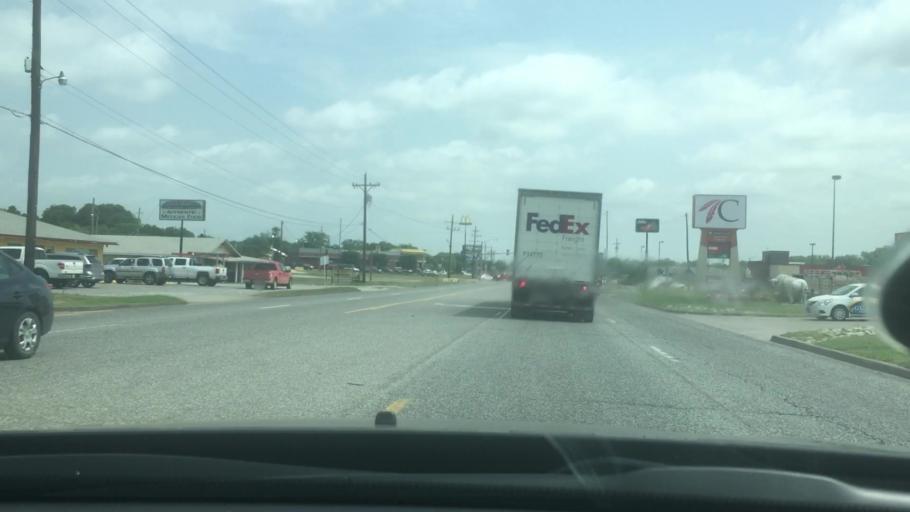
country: US
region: Oklahoma
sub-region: Atoka County
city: Atoka
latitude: 34.3728
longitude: -96.1361
